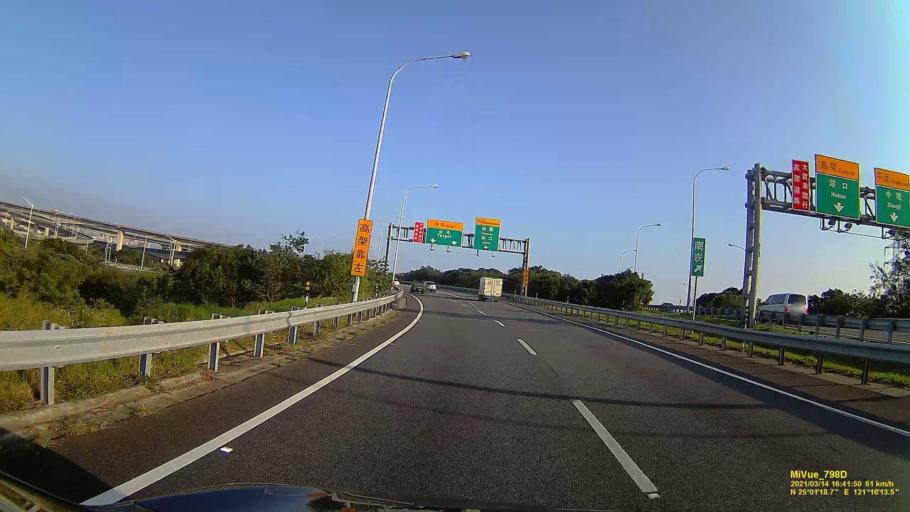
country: TW
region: Taiwan
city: Taoyuan City
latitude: 25.0217
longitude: 121.2708
